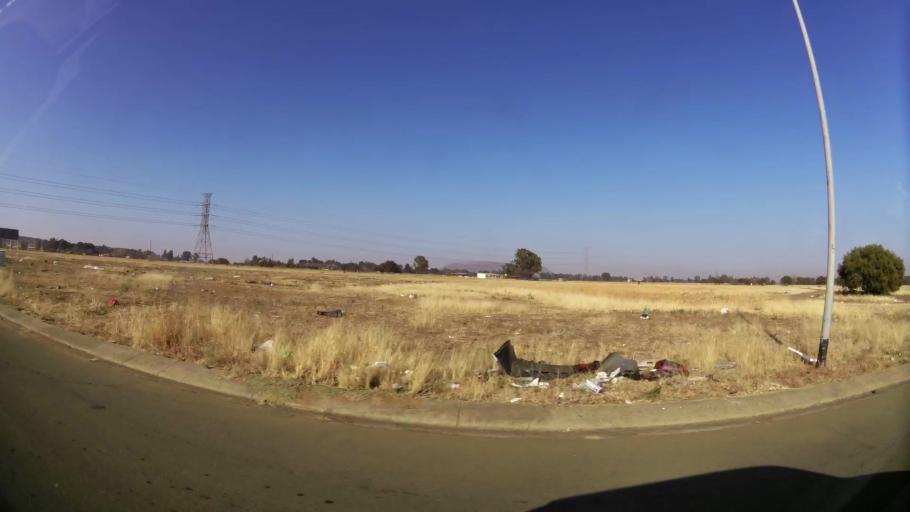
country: ZA
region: Orange Free State
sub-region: Mangaung Metropolitan Municipality
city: Bloemfontein
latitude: -29.1852
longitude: 26.1844
